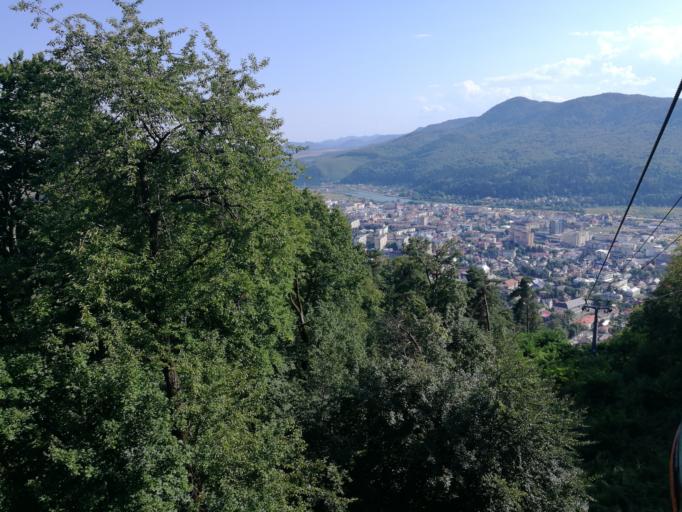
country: RO
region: Neamt
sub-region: Comuna Garcina
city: Garcina
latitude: 46.9417
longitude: 26.3661
